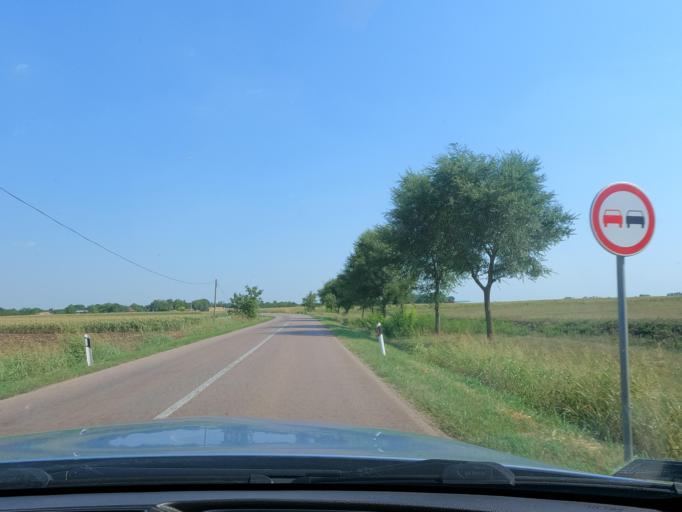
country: RS
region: Autonomna Pokrajina Vojvodina
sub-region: Severnobacki Okrug
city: Mali Igos
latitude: 45.7659
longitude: 19.7412
